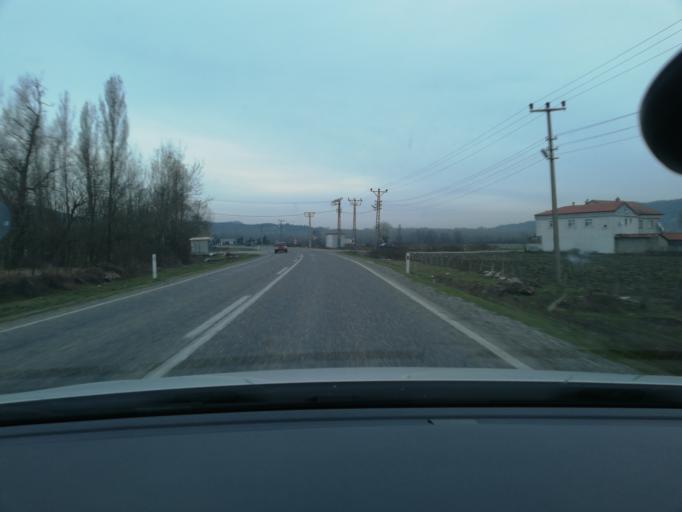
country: TR
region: Zonguldak
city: Saltukova
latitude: 41.5119
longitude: 32.1028
